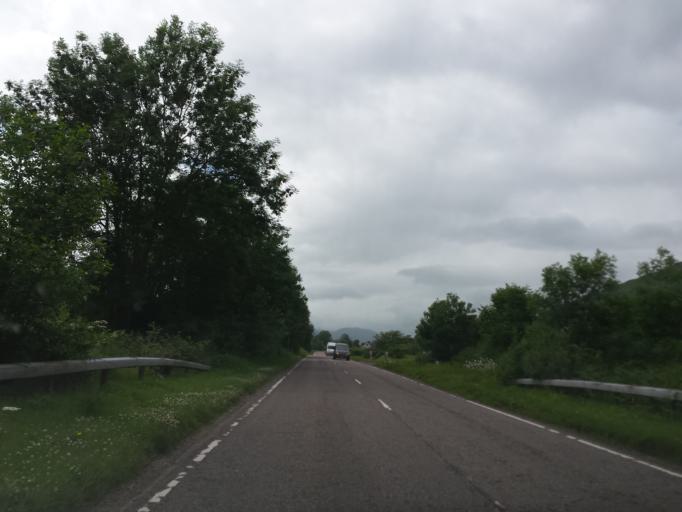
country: GB
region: Scotland
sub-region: Highland
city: Fort William
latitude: 56.8553
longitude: -5.2763
